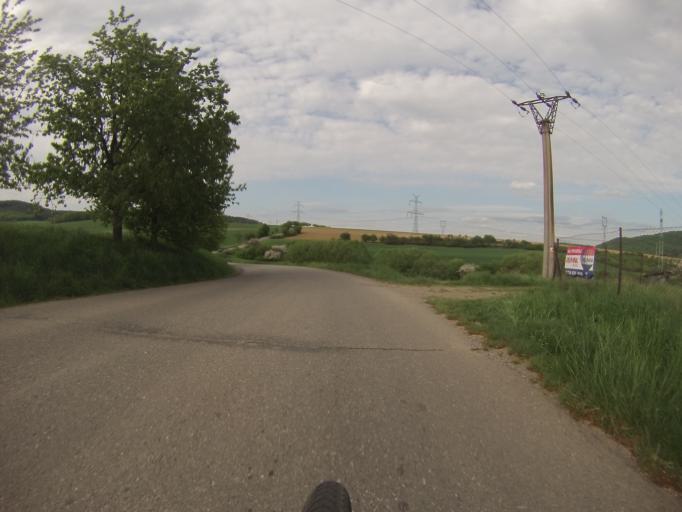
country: CZ
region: South Moravian
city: Veverska Bityska
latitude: 49.2834
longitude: 16.4438
